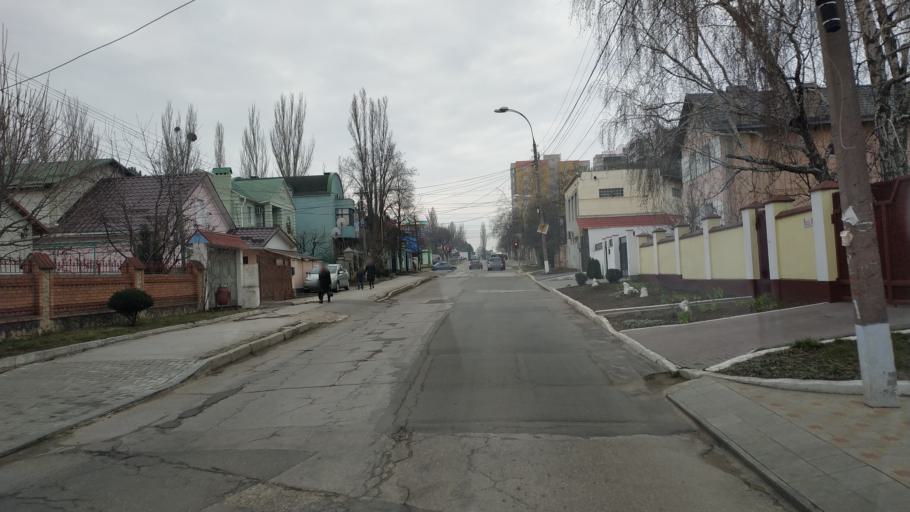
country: MD
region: Chisinau
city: Vatra
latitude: 47.0331
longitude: 28.7831
